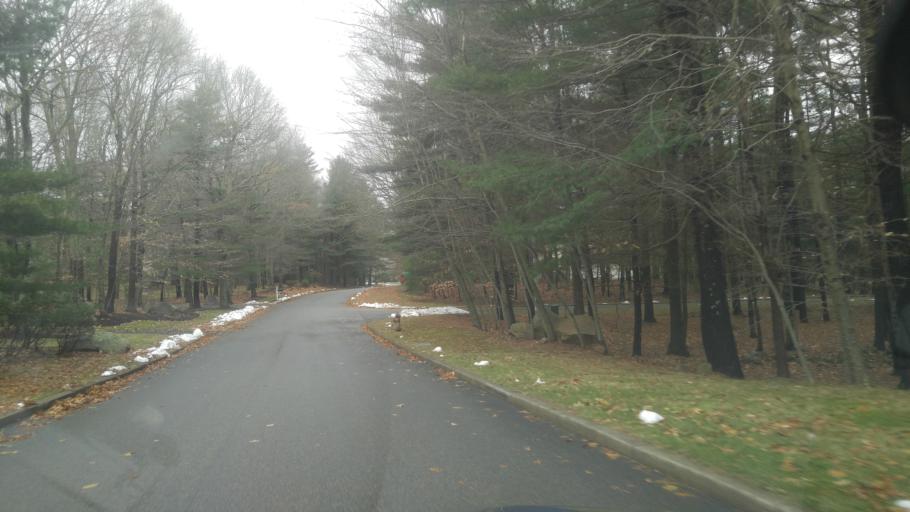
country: US
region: Rhode Island
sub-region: Kent County
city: West Warwick
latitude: 41.6481
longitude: -71.5342
